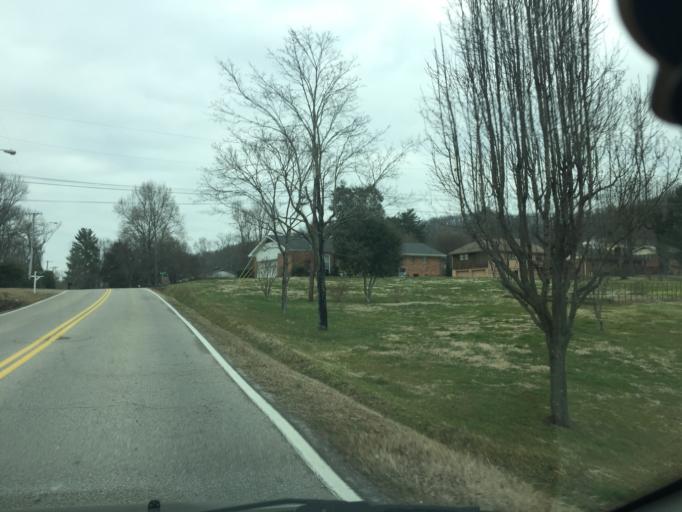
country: US
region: Tennessee
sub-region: Hamilton County
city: East Brainerd
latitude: 35.0095
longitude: -85.1281
